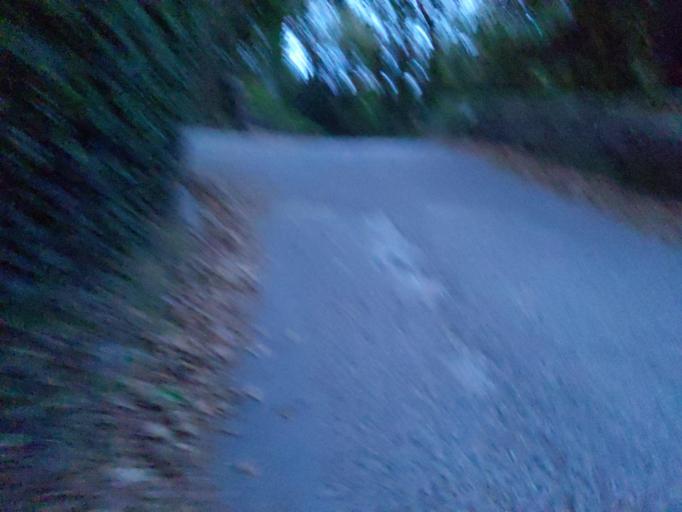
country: GB
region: England
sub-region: Devon
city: Salcombe
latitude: 50.2278
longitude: -3.7826
